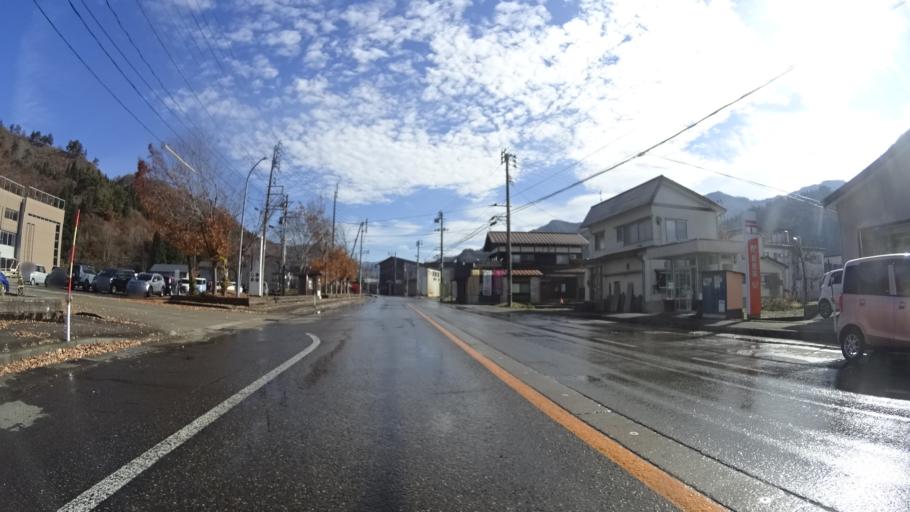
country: JP
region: Niigata
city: Muikamachi
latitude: 37.2261
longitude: 139.0076
